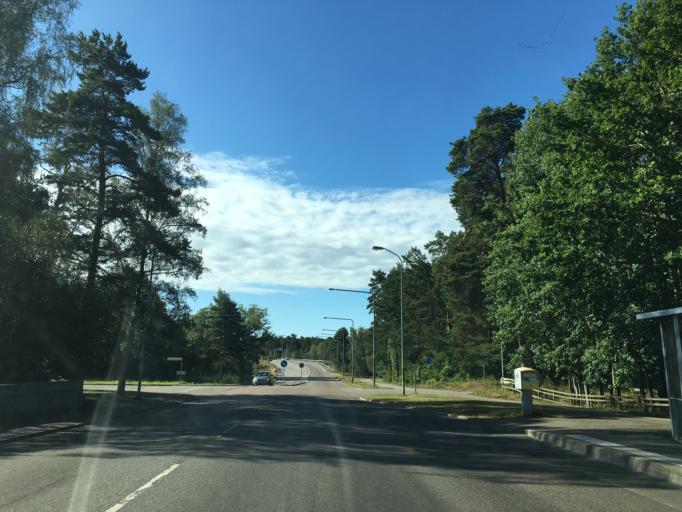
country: SE
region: Kalmar
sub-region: Kalmar Kommun
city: Kalmar
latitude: 56.6879
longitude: 16.3555
